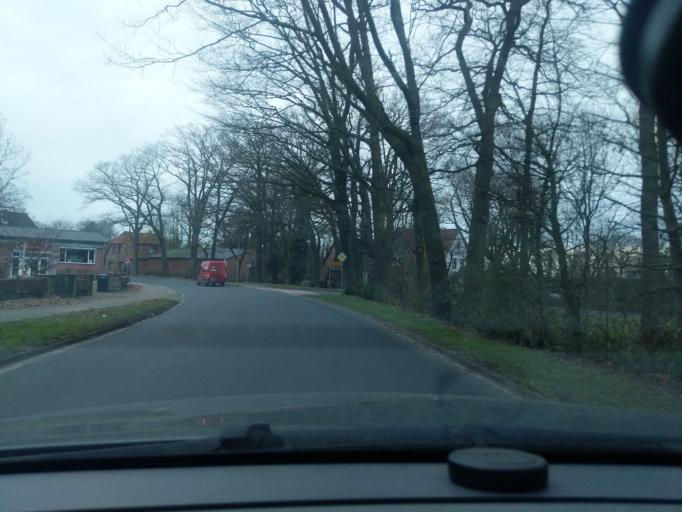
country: DE
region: Lower Saxony
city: Helvesiek
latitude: 53.2155
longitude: 9.4911
